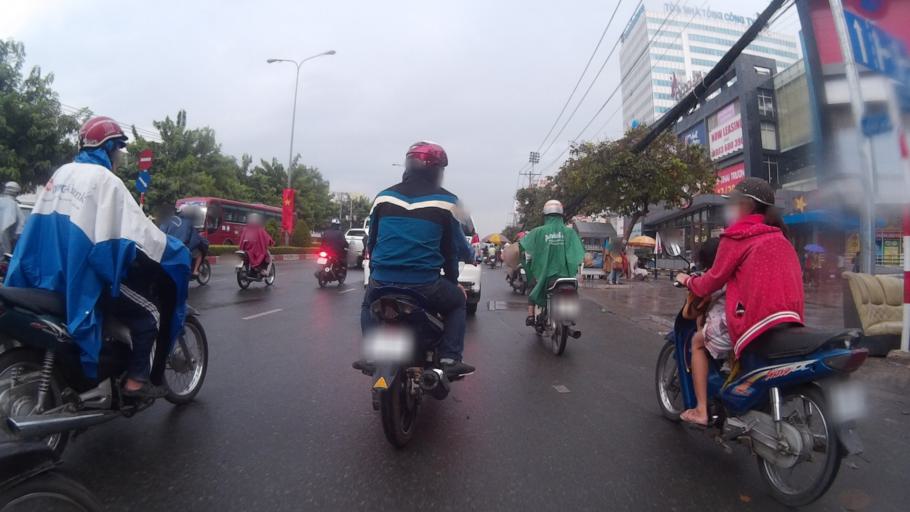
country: VN
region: Ho Chi Minh City
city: Quan Tan Phu
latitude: 10.8013
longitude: 106.6525
